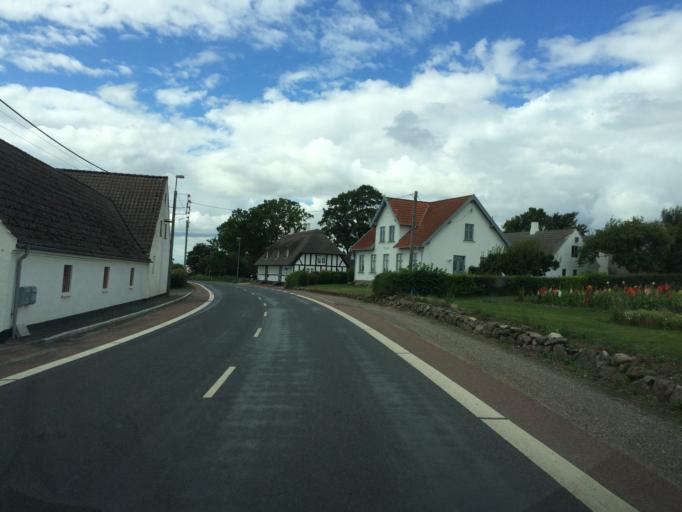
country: DK
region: South Denmark
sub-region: Assens Kommune
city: Harby
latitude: 55.1560
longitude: 10.1462
